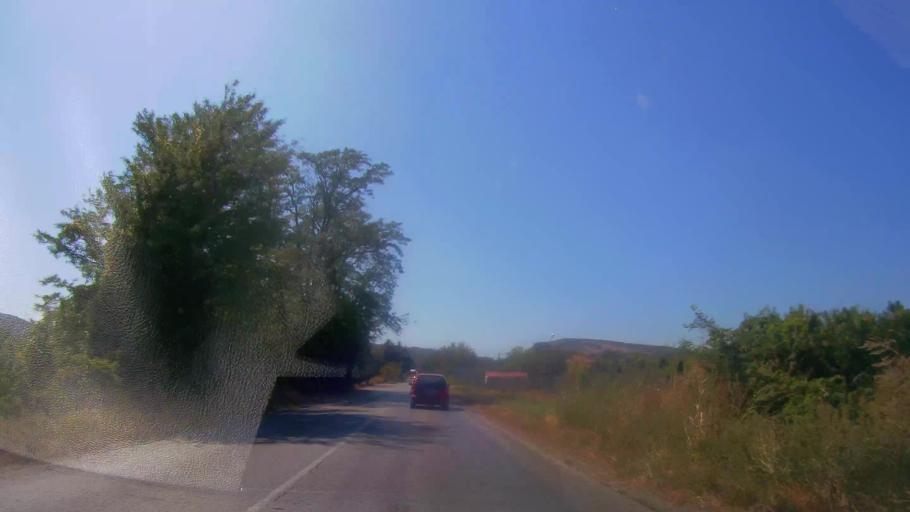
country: BG
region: Veliko Turnovo
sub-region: Obshtina Gorna Oryakhovitsa
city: Purvomaytsi
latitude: 43.1487
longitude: 25.6153
